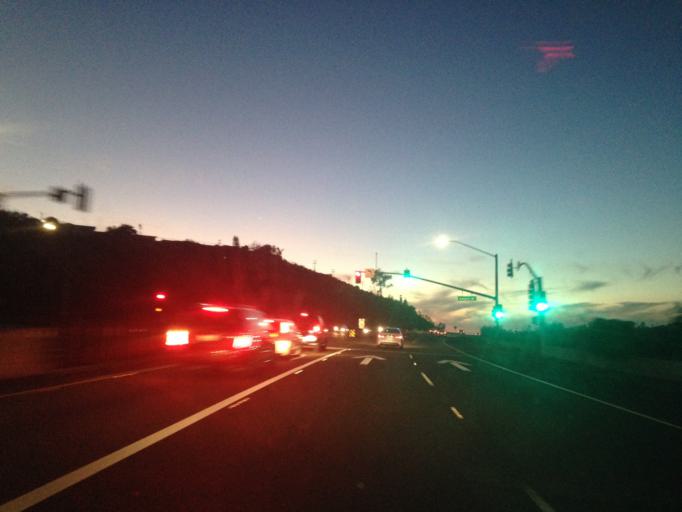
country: US
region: California
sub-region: San Diego County
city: Camp Pendleton South
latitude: 33.2126
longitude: -117.3668
